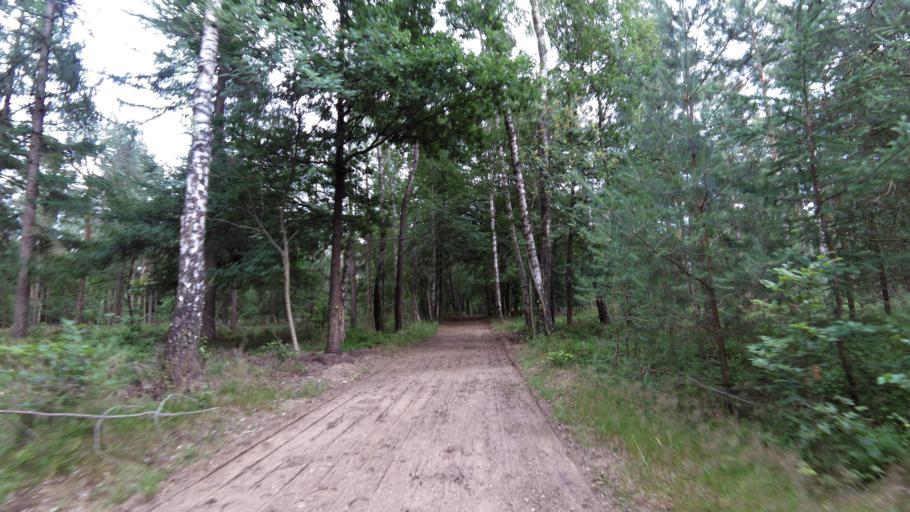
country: NL
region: Gelderland
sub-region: Gemeente Apeldoorn
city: Apeldoorn
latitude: 52.1949
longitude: 5.9066
